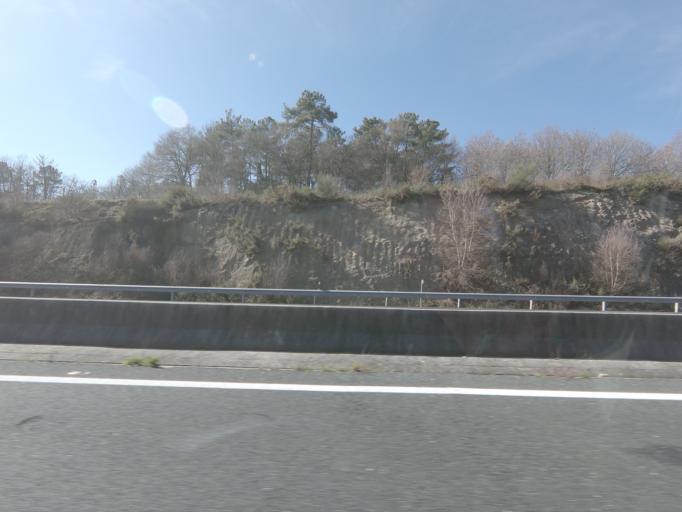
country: ES
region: Galicia
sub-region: Provincia de Ourense
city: Pinor
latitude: 42.5180
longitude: -8.0194
